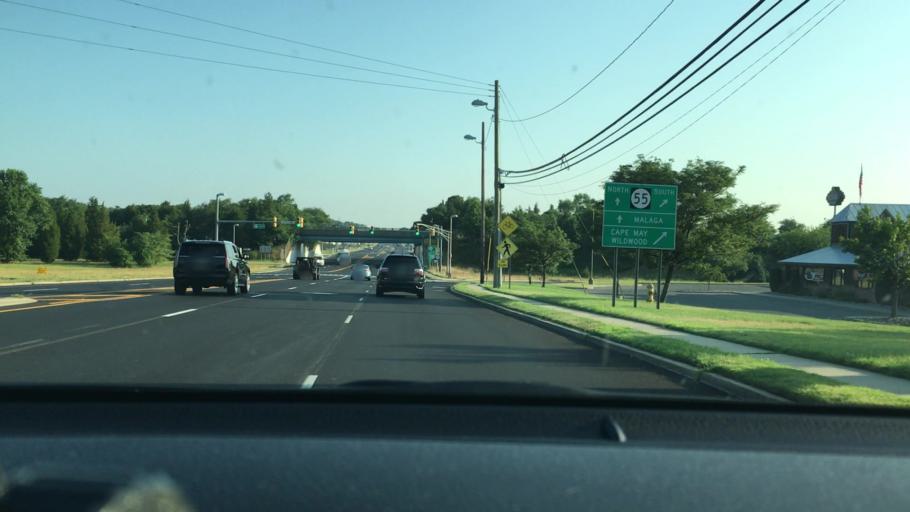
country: US
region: New Jersey
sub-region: Cumberland County
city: South Vineland
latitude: 39.4263
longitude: -75.0398
